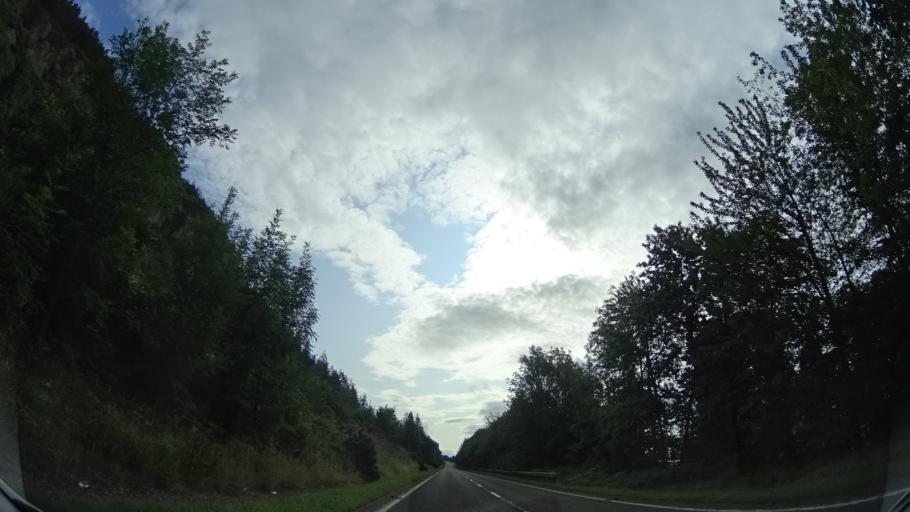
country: GB
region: Scotland
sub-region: Highland
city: Muir of Ord
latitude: 57.5584
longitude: -4.5197
